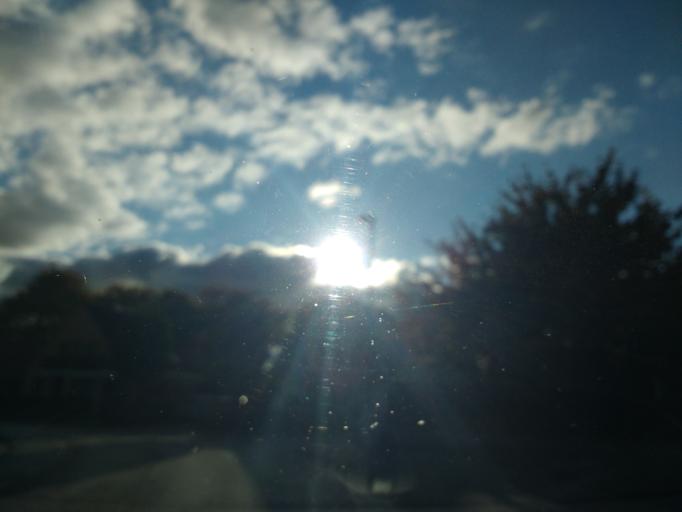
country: DE
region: Schleswig-Holstein
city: Gromitz
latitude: 54.1493
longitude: 10.9541
